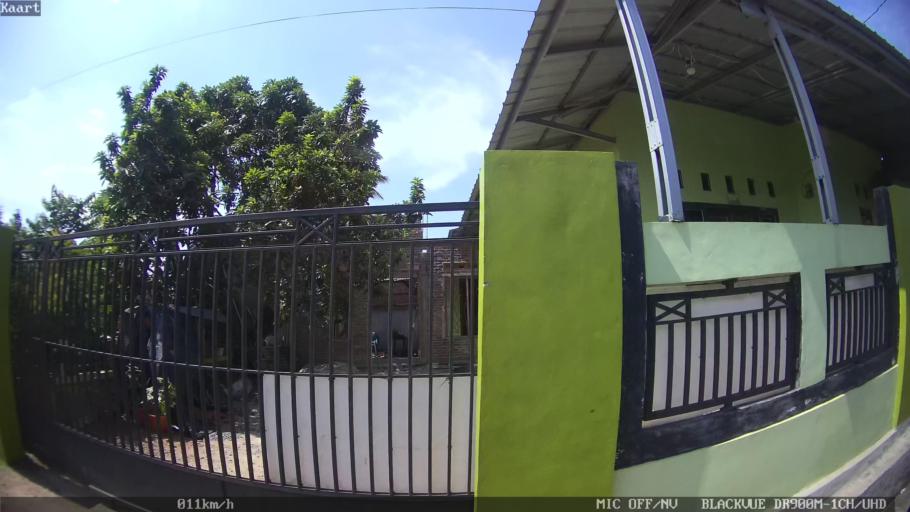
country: ID
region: Lampung
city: Kedaton
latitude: -5.3687
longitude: 105.2529
